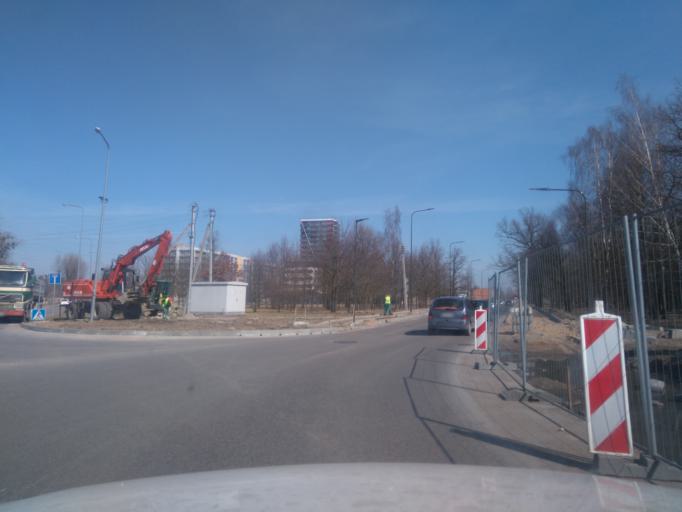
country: LT
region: Kauno apskritis
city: Dainava (Kaunas)
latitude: 54.8812
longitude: 23.9482
